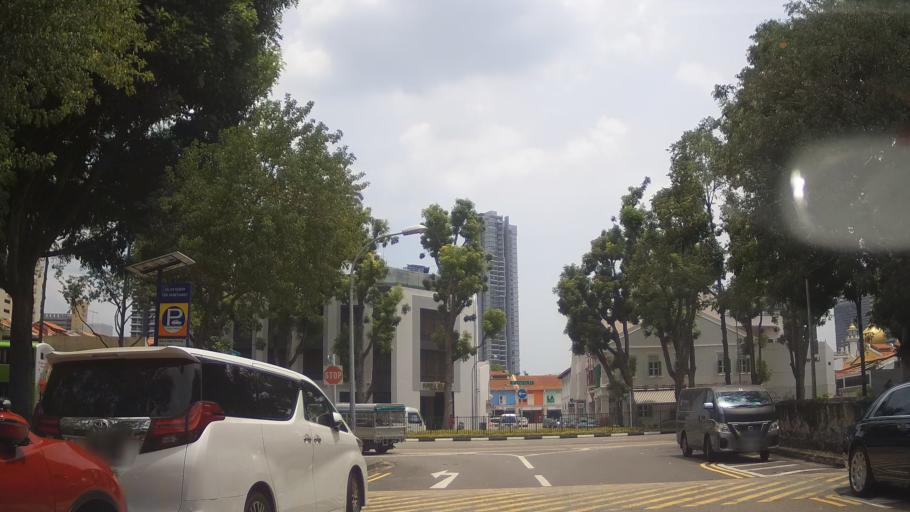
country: SG
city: Singapore
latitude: 1.3043
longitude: 103.8587
